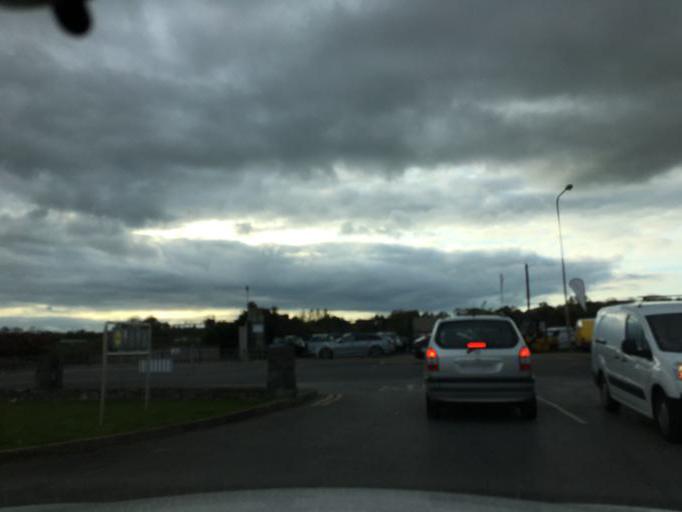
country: IE
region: Leinster
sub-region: Loch Garman
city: New Ross
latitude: 52.3919
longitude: -6.9492
